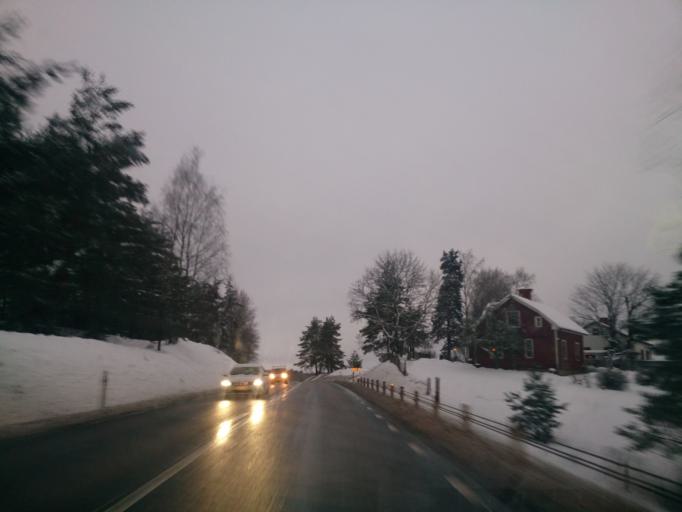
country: SE
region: OEstergoetland
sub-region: Linkopings Kommun
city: Sturefors
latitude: 58.3174
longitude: 15.8709
